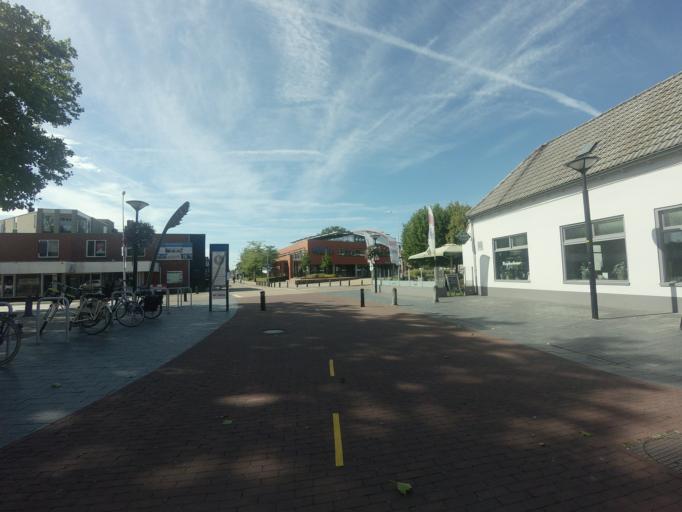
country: NL
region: Overijssel
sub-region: Gemeente Raalte
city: Raalte
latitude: 52.3845
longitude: 6.2757
